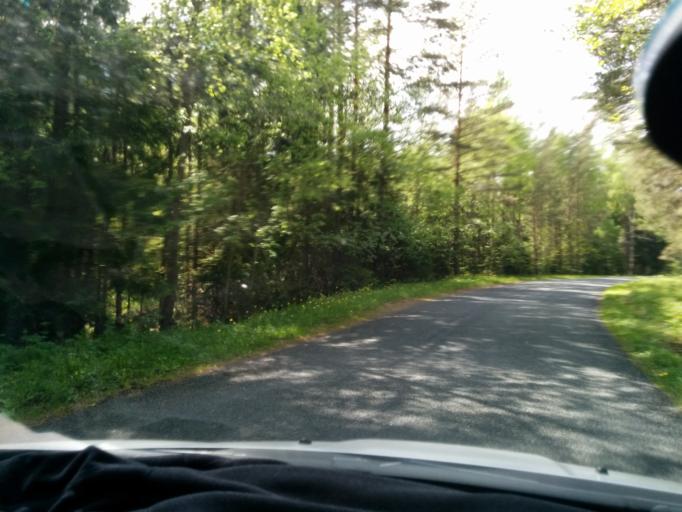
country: EE
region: Harju
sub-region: Loksa linn
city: Loksa
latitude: 59.5631
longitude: 25.6454
